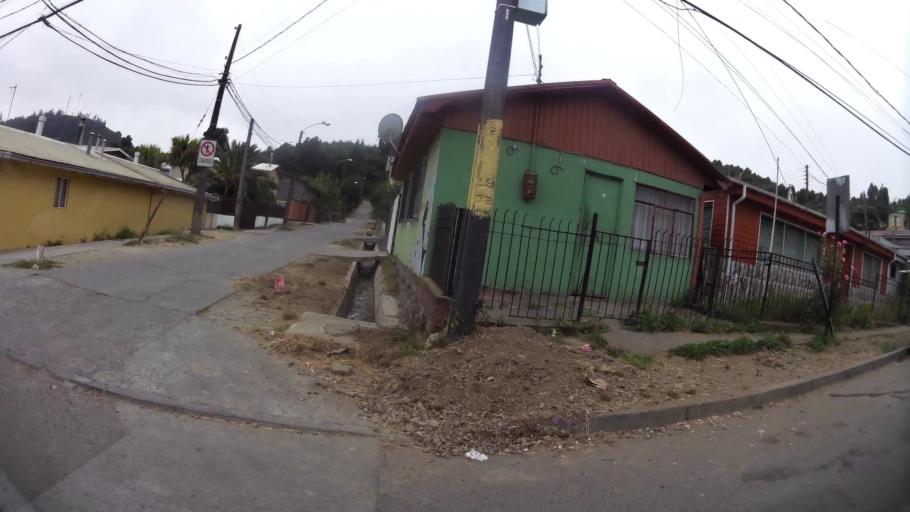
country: CL
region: Biobio
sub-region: Provincia de Concepcion
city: Concepcion
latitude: -36.8363
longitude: -73.0004
